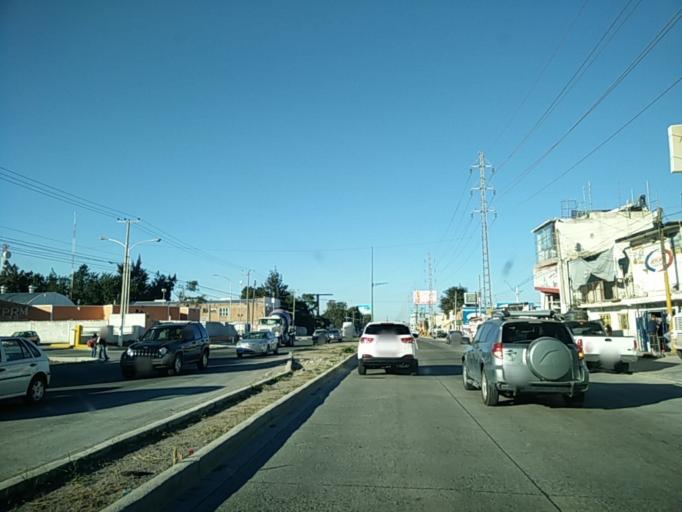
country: MX
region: Jalisco
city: Nuevo Mexico
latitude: 20.7102
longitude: -103.4578
